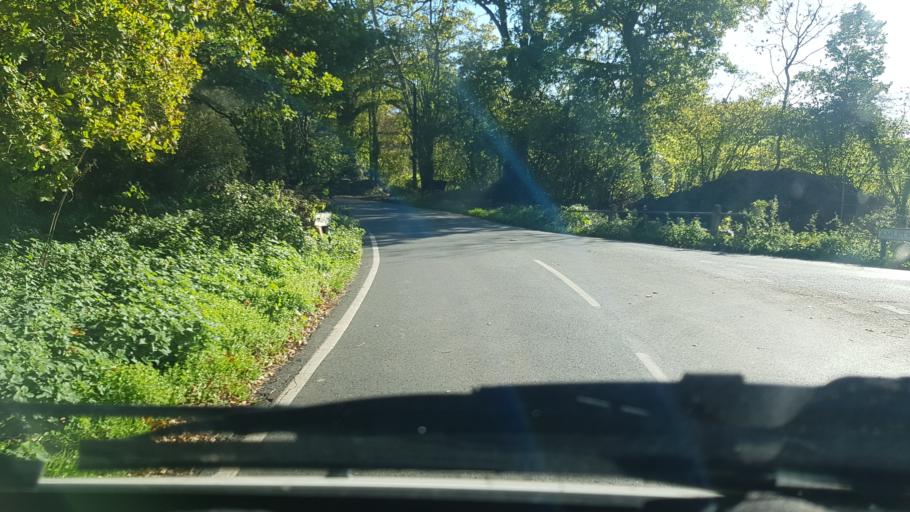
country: GB
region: England
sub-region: Surrey
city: Cranleigh
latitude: 51.1521
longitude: -0.4887
